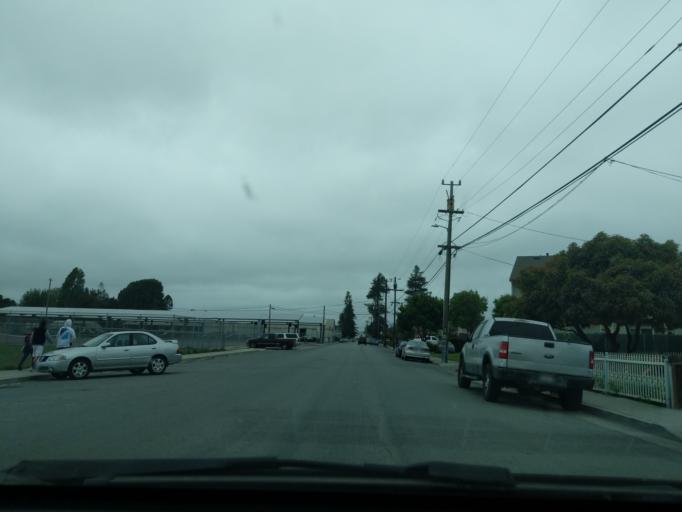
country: US
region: California
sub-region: Monterey County
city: Pajaro
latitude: 36.9137
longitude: -121.7477
